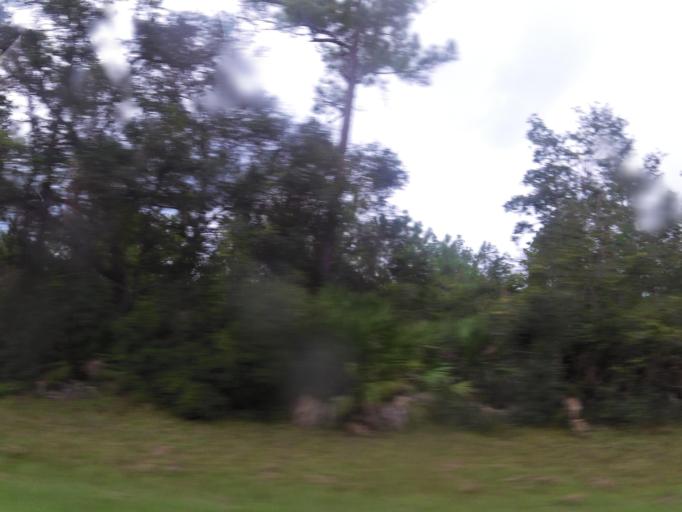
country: US
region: Florida
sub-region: Flagler County
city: Bunnell
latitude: 29.5041
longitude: -81.3294
